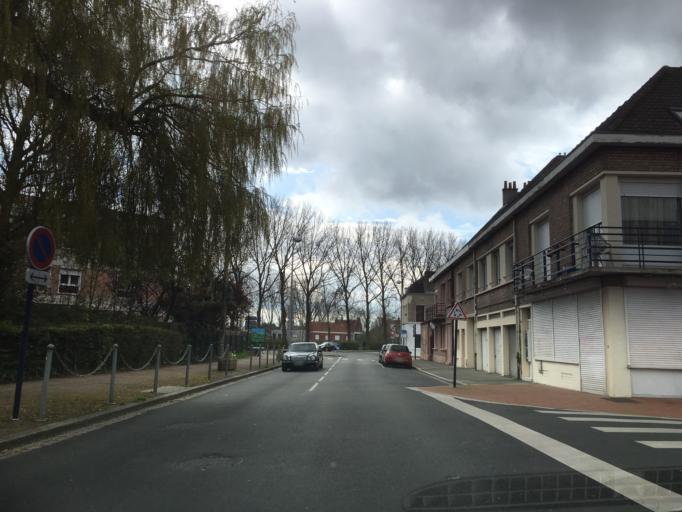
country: FR
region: Nord-Pas-de-Calais
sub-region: Departement du Nord
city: Dunkerque
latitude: 51.0321
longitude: 2.3816
